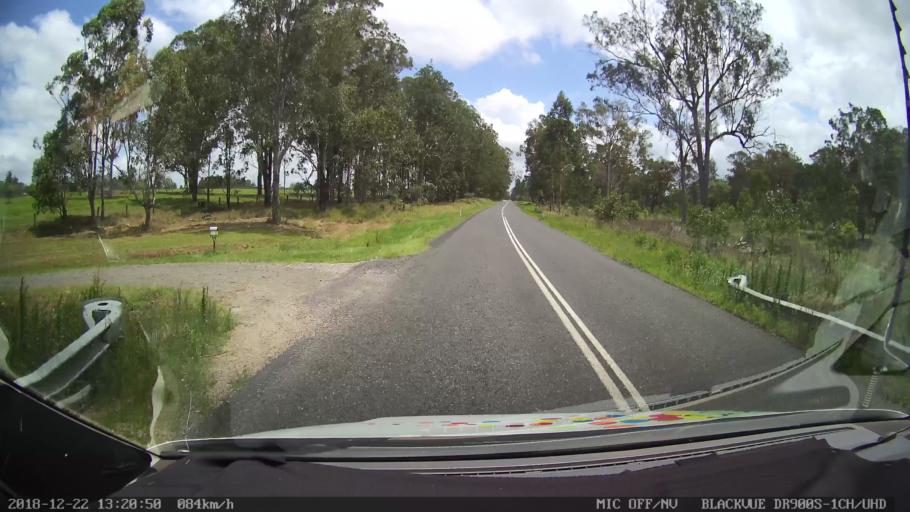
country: AU
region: New South Wales
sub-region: Clarence Valley
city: South Grafton
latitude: -29.7709
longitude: 152.9257
